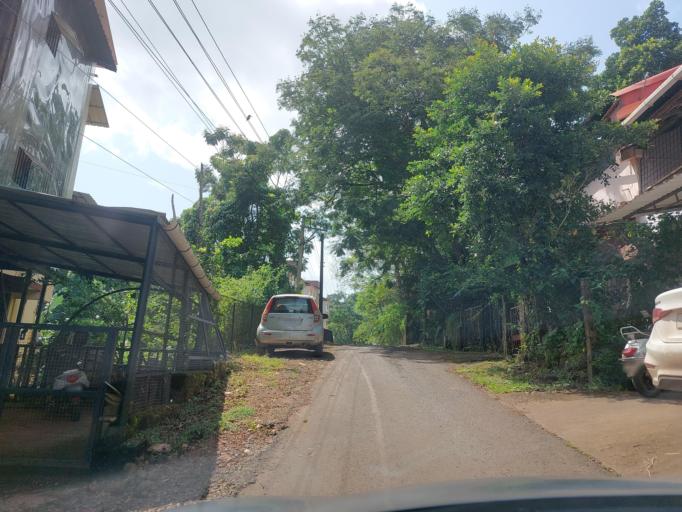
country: IN
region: Goa
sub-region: North Goa
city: Queula
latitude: 15.3971
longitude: 73.9996
